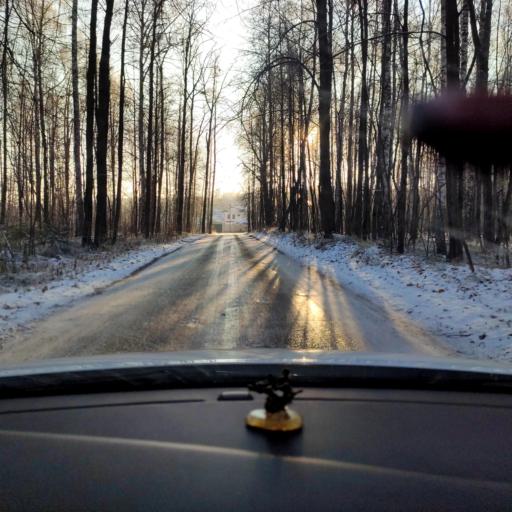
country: RU
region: Tatarstan
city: Stolbishchi
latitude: 55.6741
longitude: 49.1046
